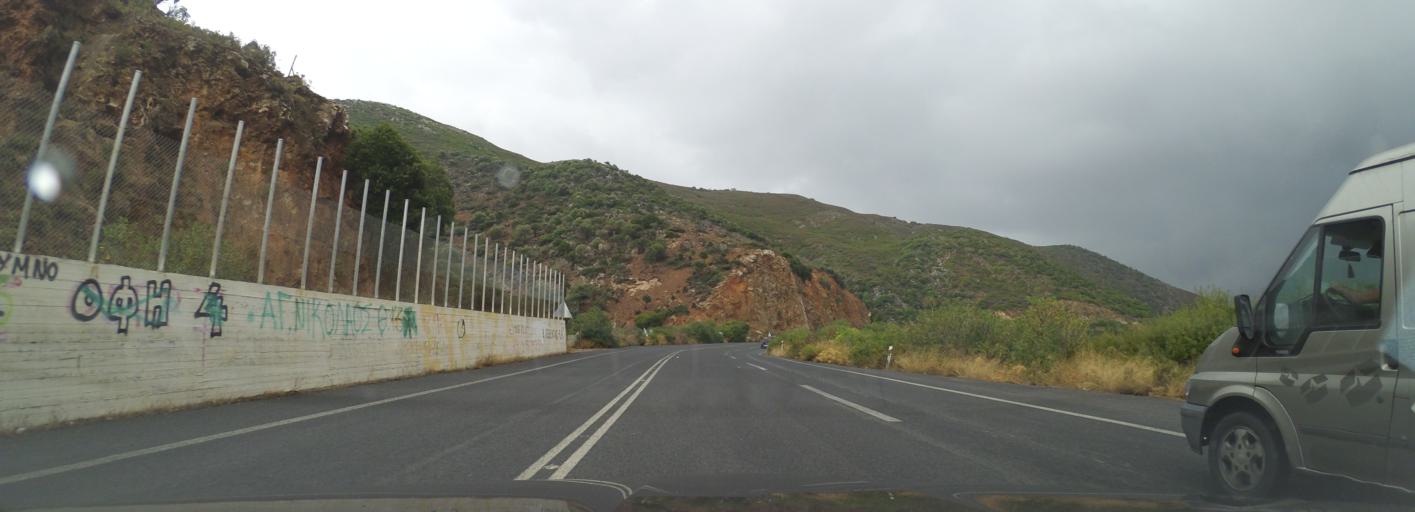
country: GR
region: Crete
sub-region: Nomos Rethymnis
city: Anogeia
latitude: 35.3888
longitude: 24.9107
